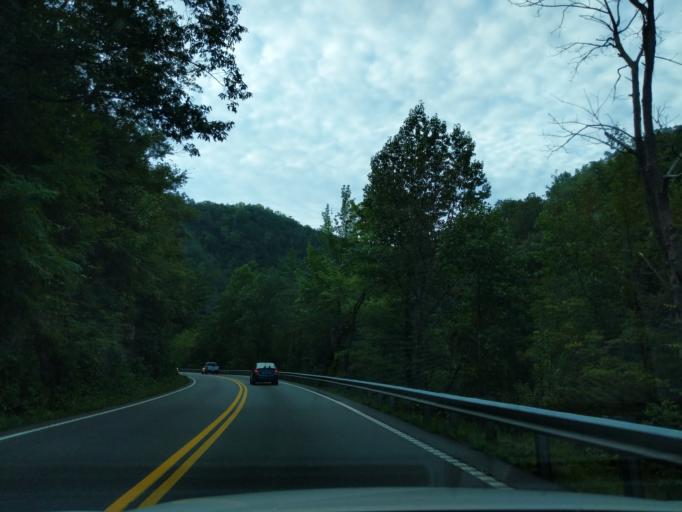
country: US
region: Georgia
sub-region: Fannin County
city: McCaysville
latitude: 35.0814
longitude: -84.5090
